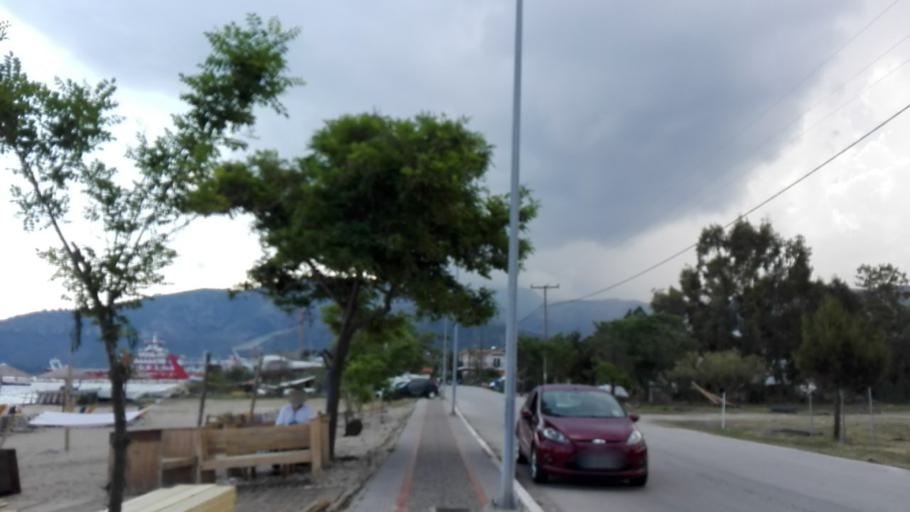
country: GR
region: East Macedonia and Thrace
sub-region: Nomos Kavalas
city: Prinos
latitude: 40.7596
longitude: 24.5725
